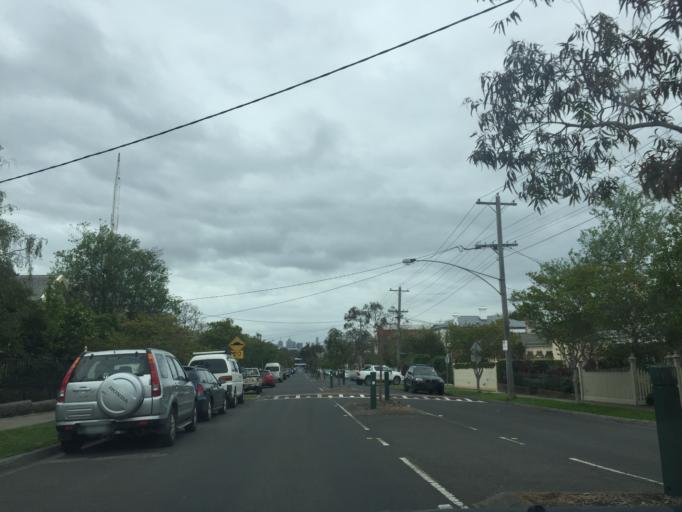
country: AU
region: Victoria
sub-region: Boroondara
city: Hawthorn East
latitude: -37.8226
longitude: 145.0505
